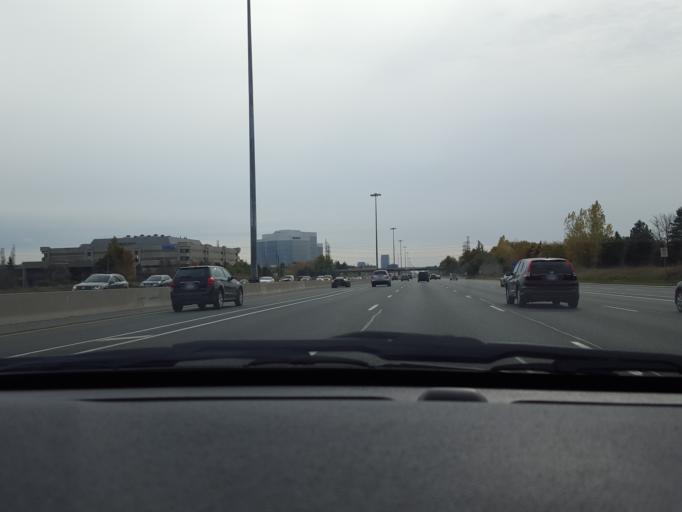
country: CA
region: Ontario
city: Willowdale
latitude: 43.8076
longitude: -79.3465
